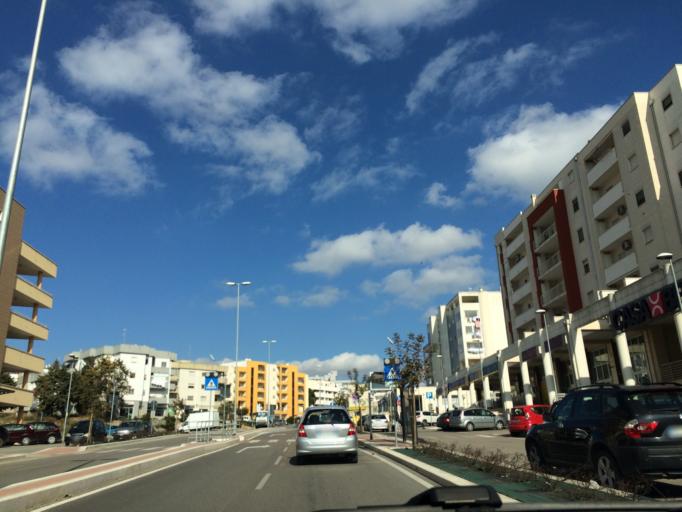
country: IT
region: Basilicate
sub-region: Provincia di Matera
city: Matera
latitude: 40.6712
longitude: 16.5838
